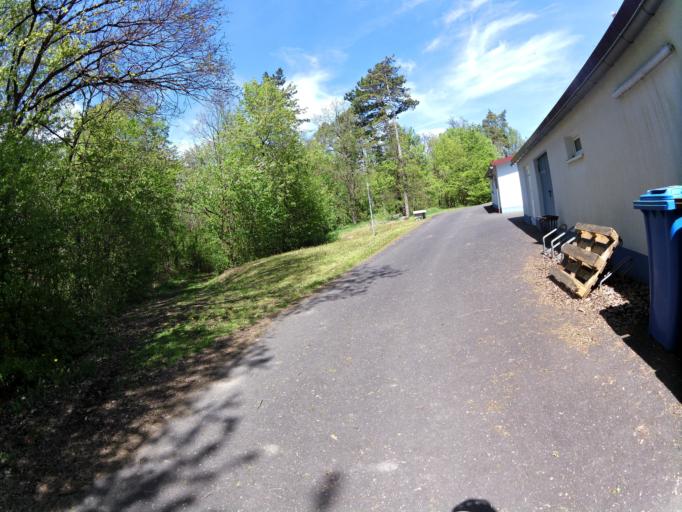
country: DE
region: Bavaria
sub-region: Regierungsbezirk Unterfranken
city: Greussenheim
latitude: 49.8204
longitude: 9.7624
